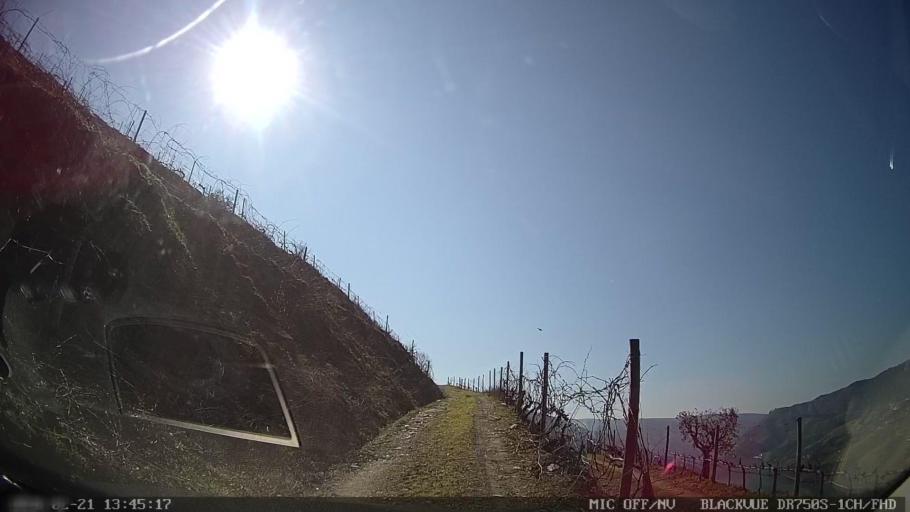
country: PT
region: Viseu
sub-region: Tabuaco
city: Tabuaco
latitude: 41.1749
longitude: -7.5446
